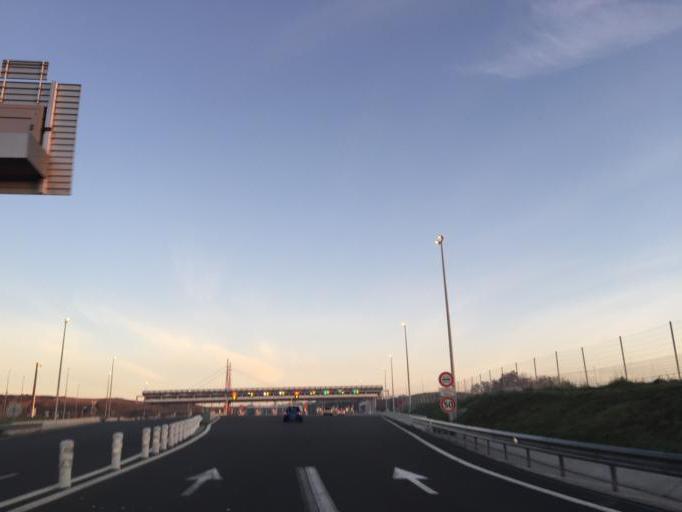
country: FR
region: Rhone-Alpes
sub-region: Departement de la Loire
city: Balbigny
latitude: 45.8390
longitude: 4.1646
